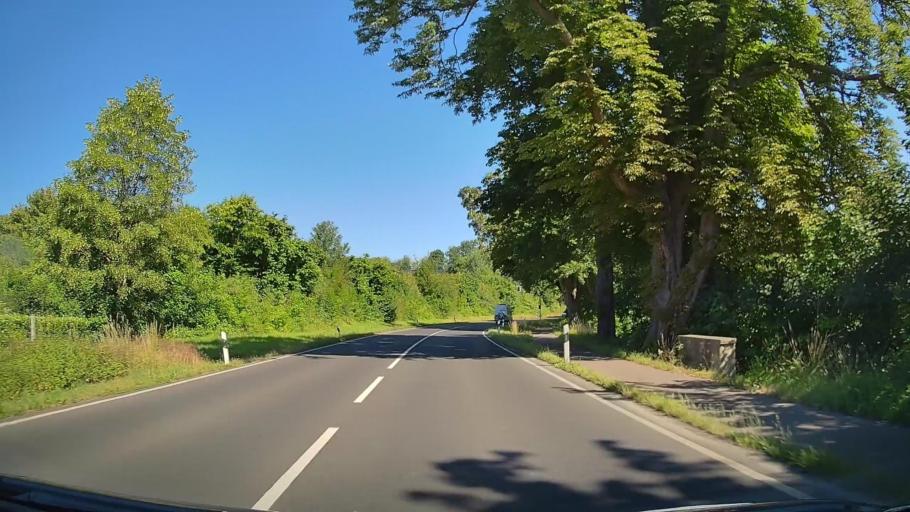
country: DE
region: Lower Saxony
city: Hameln
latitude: 52.0656
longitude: 9.3512
